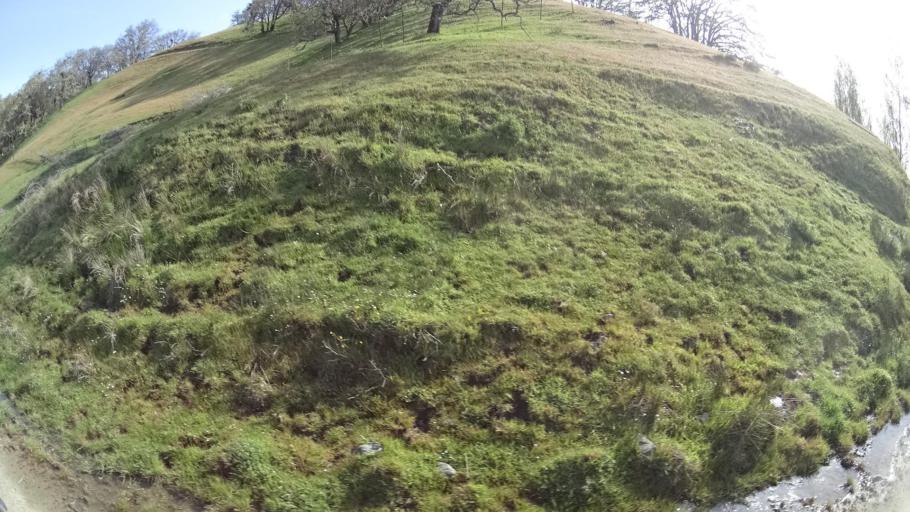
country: US
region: California
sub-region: Humboldt County
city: Hydesville
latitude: 40.6427
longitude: -123.9171
